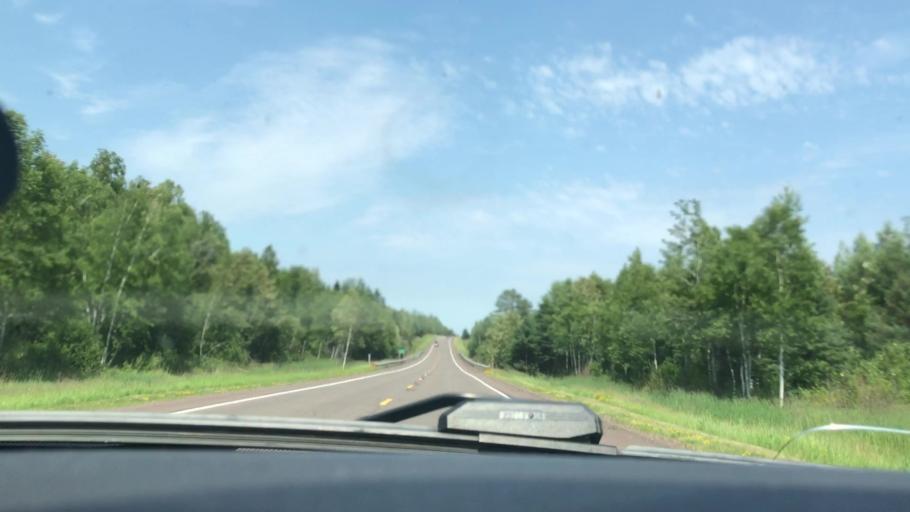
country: US
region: Minnesota
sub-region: Lake County
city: Silver Bay
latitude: 47.4427
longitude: -91.0707
